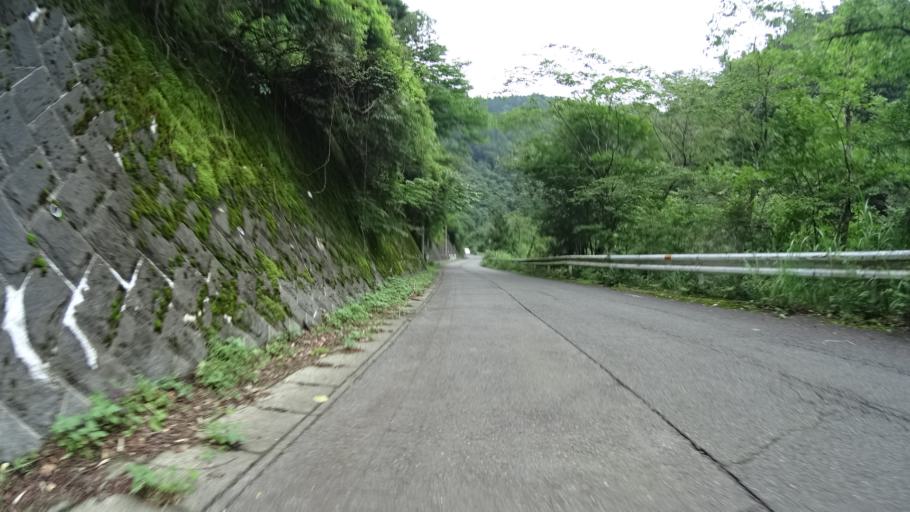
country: JP
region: Kanagawa
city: Hadano
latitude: 35.4636
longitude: 139.2151
